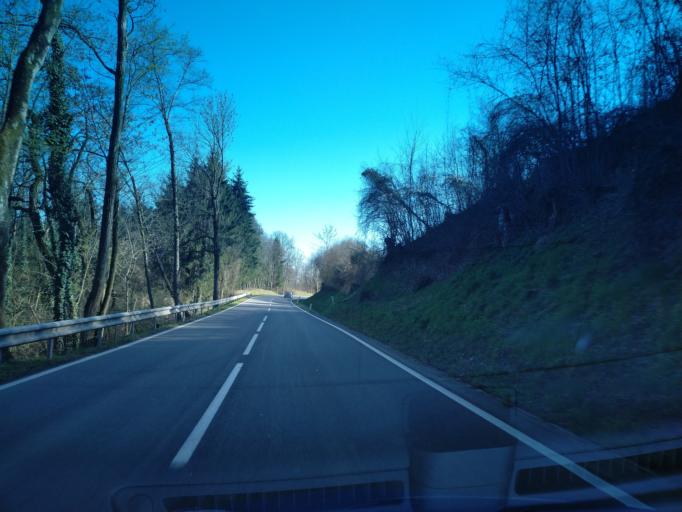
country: AT
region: Styria
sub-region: Politischer Bezirk Leibnitz
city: Stocking
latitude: 46.8737
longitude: 15.5297
